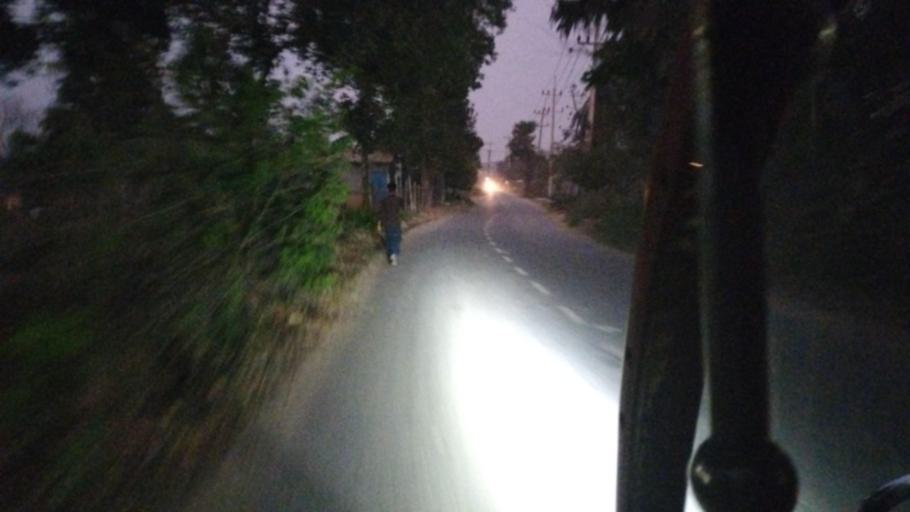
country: BD
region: Dhaka
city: Sakhipur
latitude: 24.3976
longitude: 90.3396
